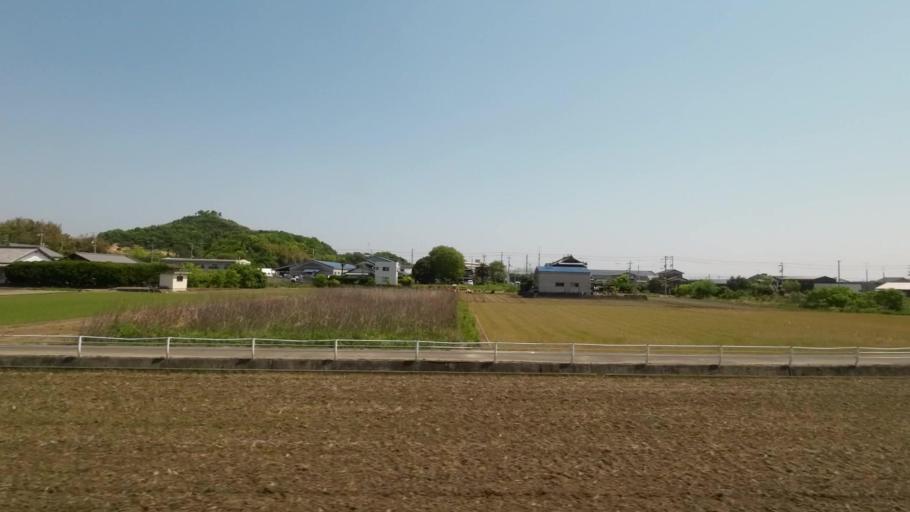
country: JP
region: Ehime
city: Saijo
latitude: 34.0193
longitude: 133.0293
